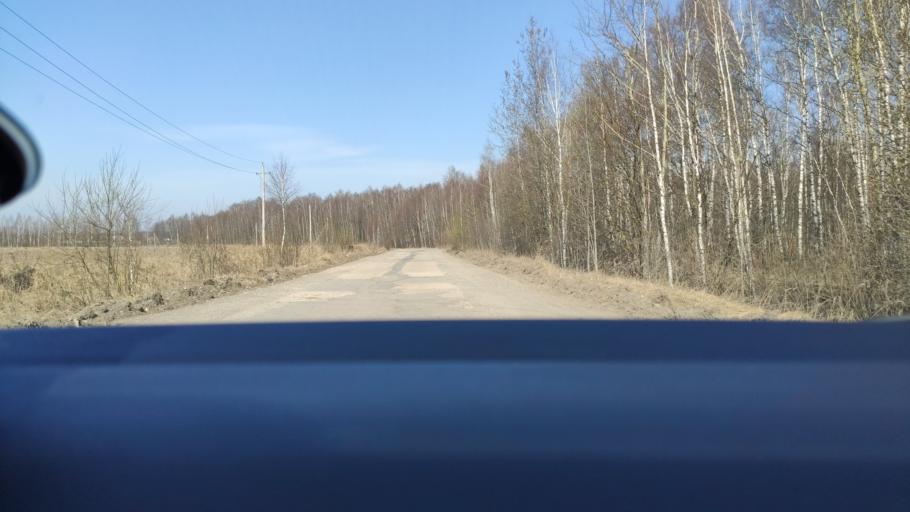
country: RU
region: Moskovskaya
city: Elektrostal'
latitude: 55.7725
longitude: 38.3812
